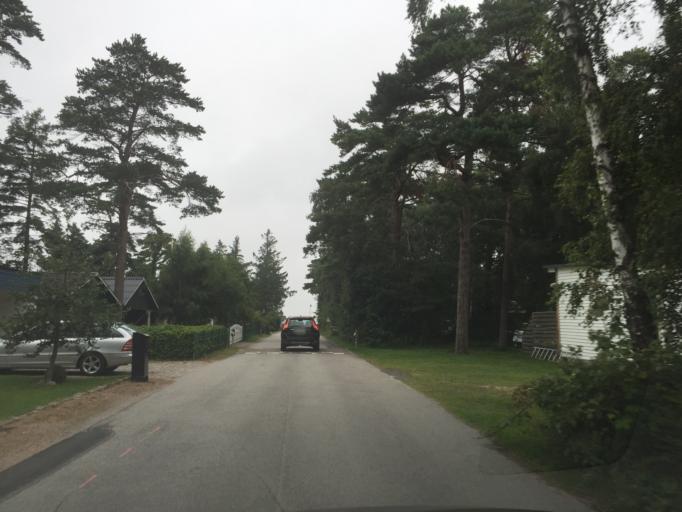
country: SE
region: Skane
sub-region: Vellinge Kommun
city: Hollviken
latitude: 55.4112
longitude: 12.9417
